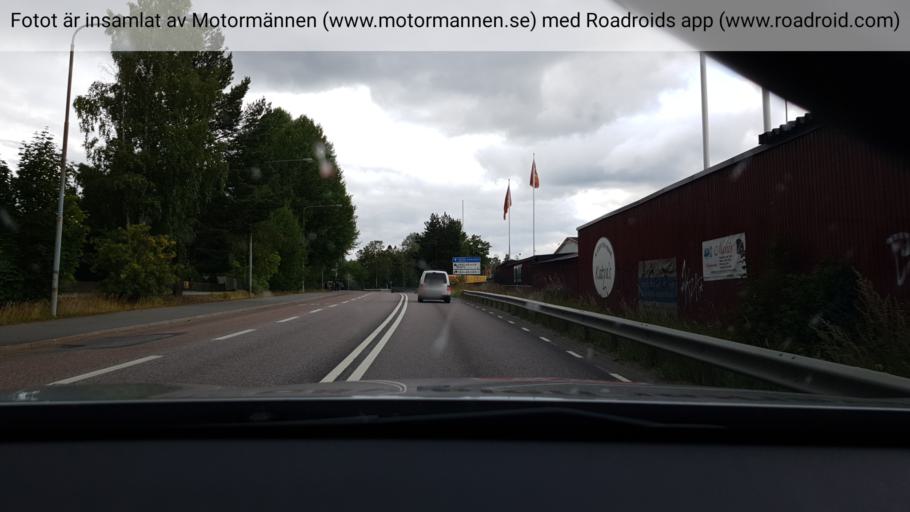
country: SE
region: Stockholm
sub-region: Tyreso Kommun
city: Bollmora
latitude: 59.2262
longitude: 18.2011
